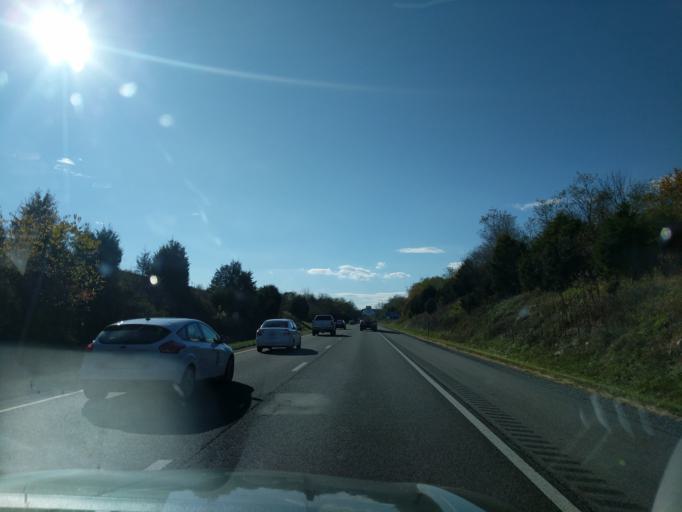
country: US
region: Virginia
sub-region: Pulaski County
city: Dublin
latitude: 37.0818
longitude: -80.6562
